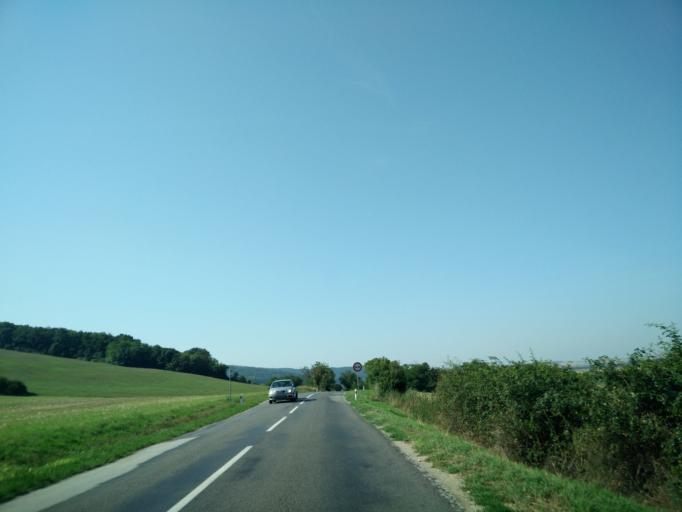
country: SK
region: Nitriansky
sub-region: Okres Nitra
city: Nitra
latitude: 48.3846
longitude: 18.0960
